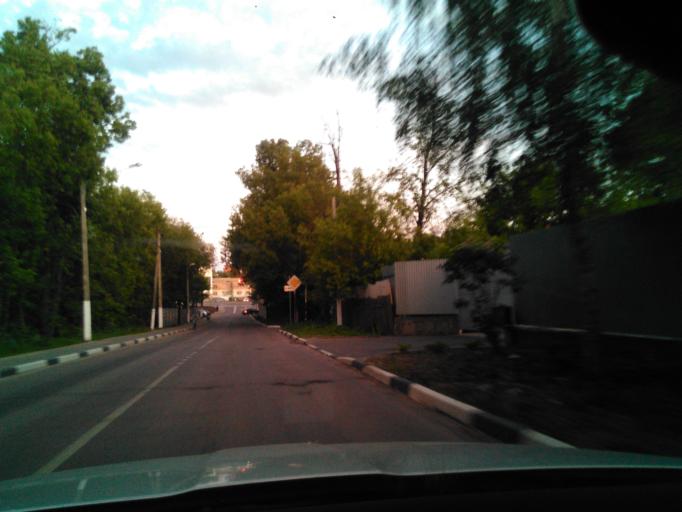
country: RU
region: Moskovskaya
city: Dolgoprudnyy
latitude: 55.9502
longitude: 37.5057
